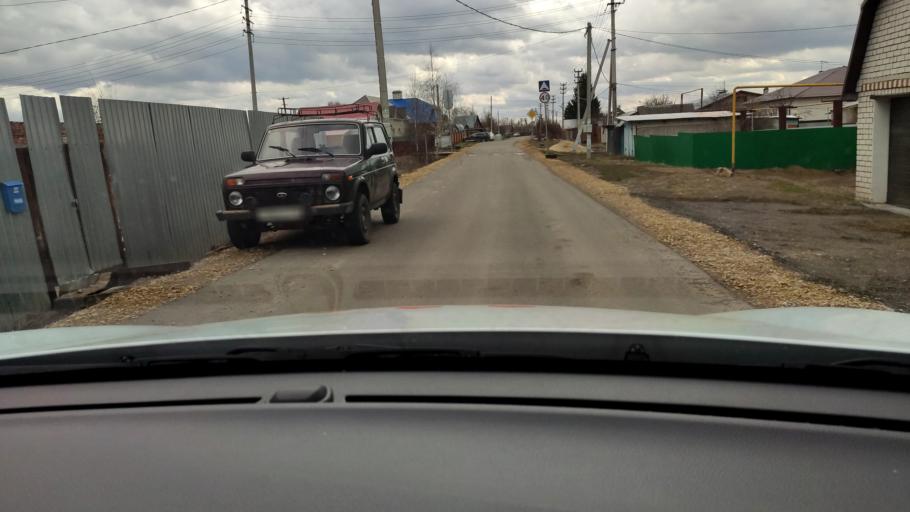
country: RU
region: Tatarstan
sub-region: Gorod Kazan'
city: Kazan
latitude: 55.8993
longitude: 49.1386
